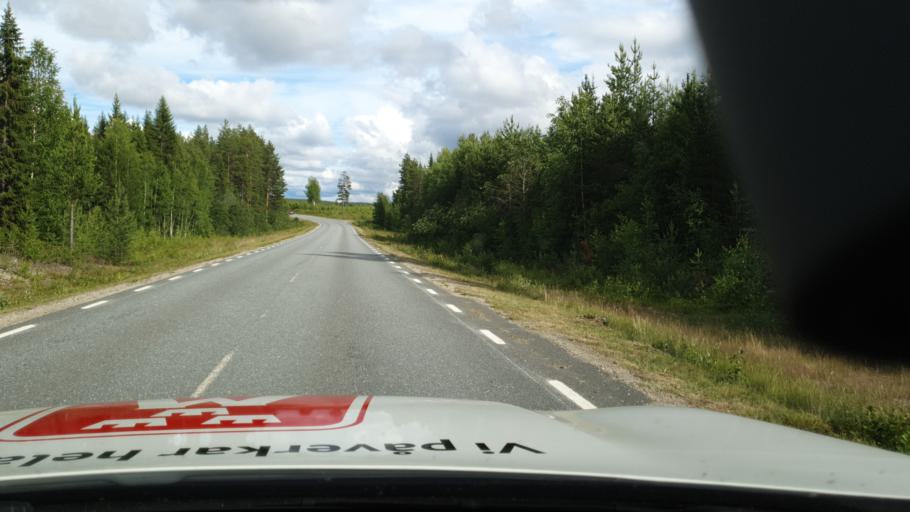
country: SE
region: Vaesterbotten
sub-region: Lycksele Kommun
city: Lycksele
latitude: 64.5045
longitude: 18.9256
